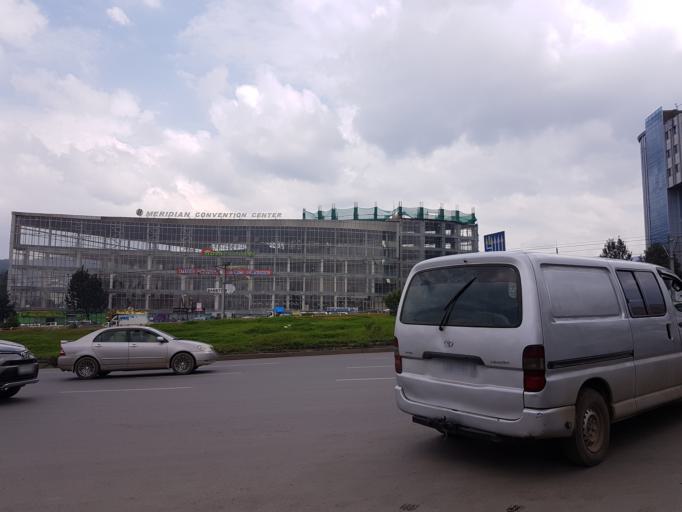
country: ET
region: Adis Abeba
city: Addis Ababa
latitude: 9.0195
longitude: 38.8263
